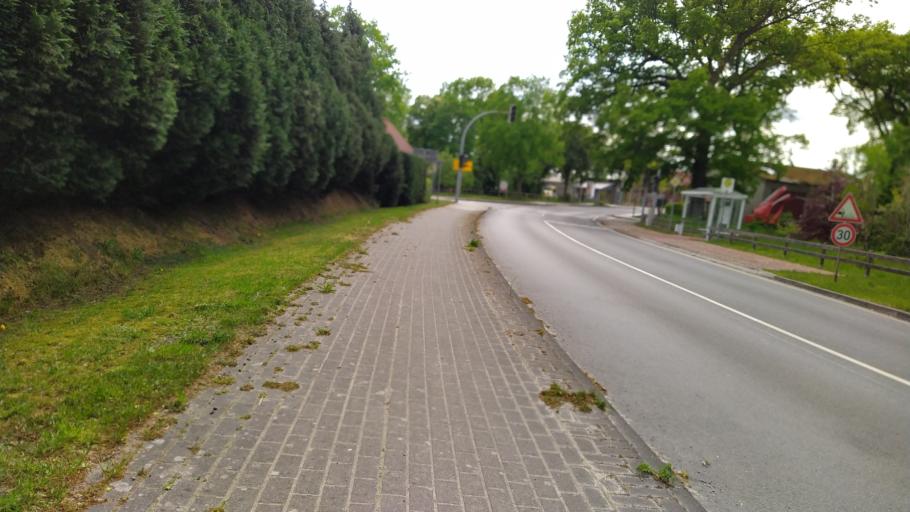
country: DE
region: Lower Saxony
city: Kirchtimke
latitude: 53.2582
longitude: 9.1841
